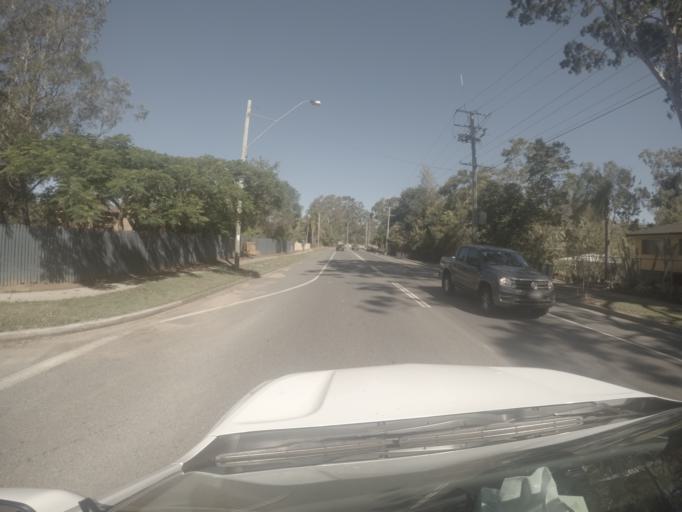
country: AU
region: Queensland
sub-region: Ipswich
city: Goodna
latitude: -27.6262
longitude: 152.9158
